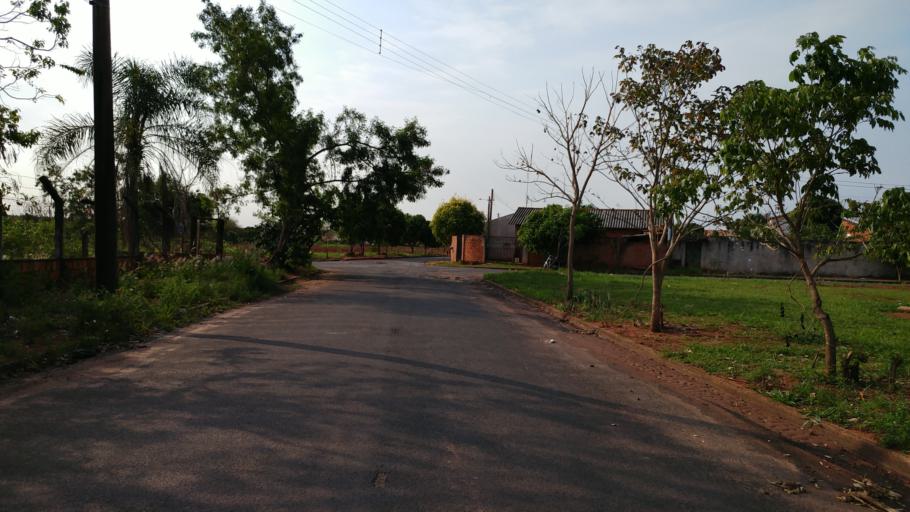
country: BR
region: Sao Paulo
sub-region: Paraguacu Paulista
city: Paraguacu Paulista
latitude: -22.4155
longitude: -50.5933
